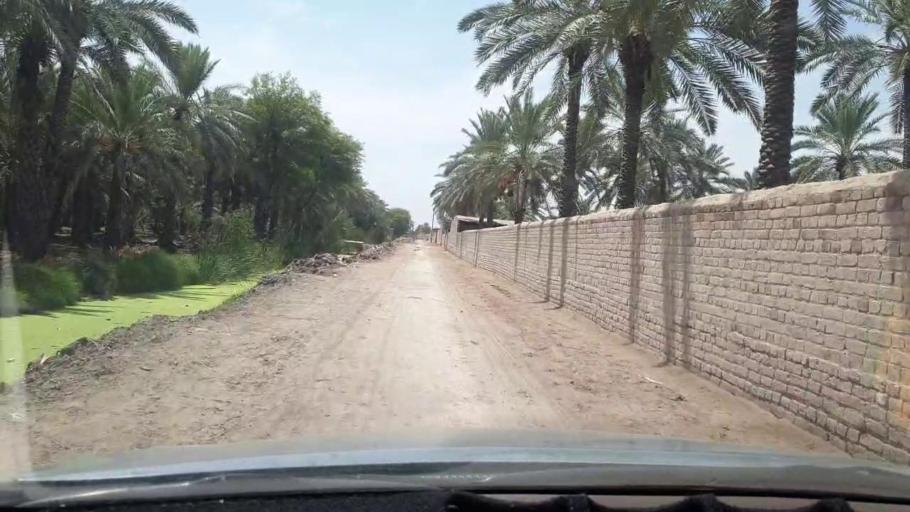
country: PK
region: Sindh
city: Khairpur
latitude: 27.4770
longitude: 68.7673
